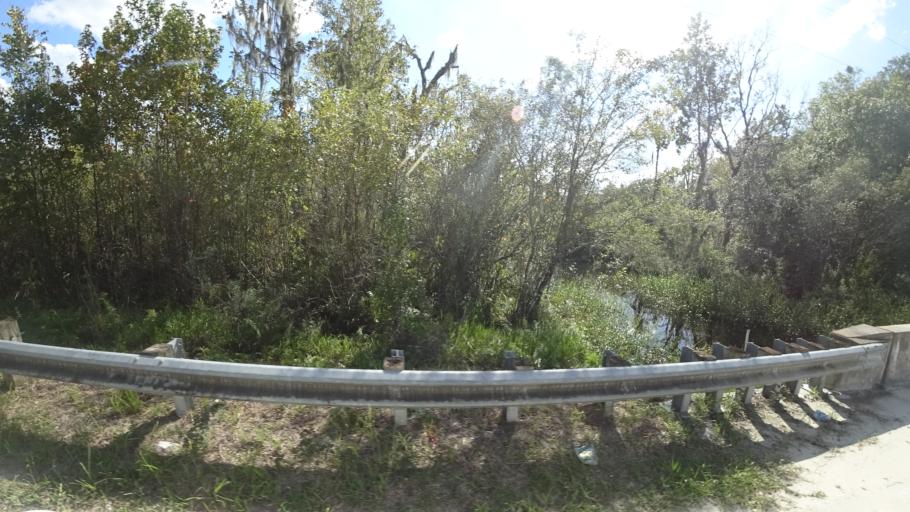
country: US
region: Florida
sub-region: Sarasota County
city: Lake Sarasota
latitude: 27.4230
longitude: -82.1411
